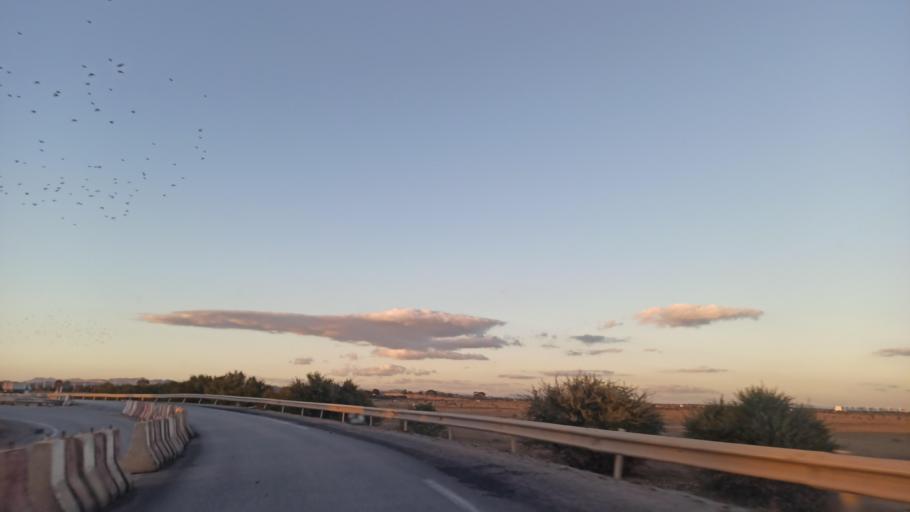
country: TN
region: Susah
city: Harqalah
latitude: 36.1084
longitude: 10.4064
